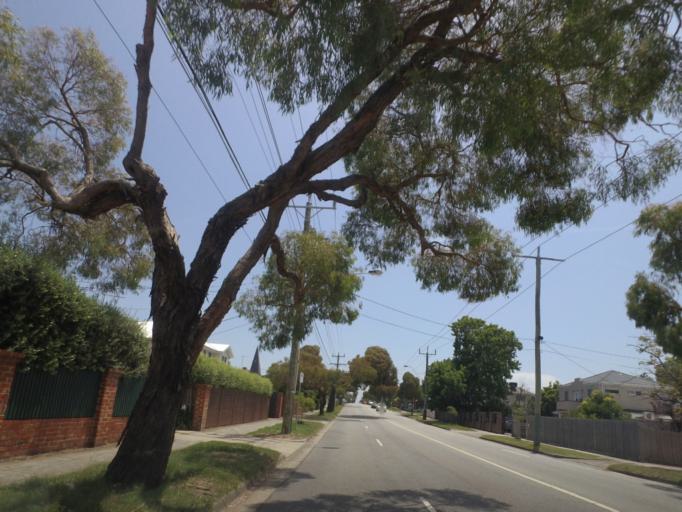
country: AU
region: Victoria
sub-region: Bayside
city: Hampton East
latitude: -37.9404
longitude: 145.0232
